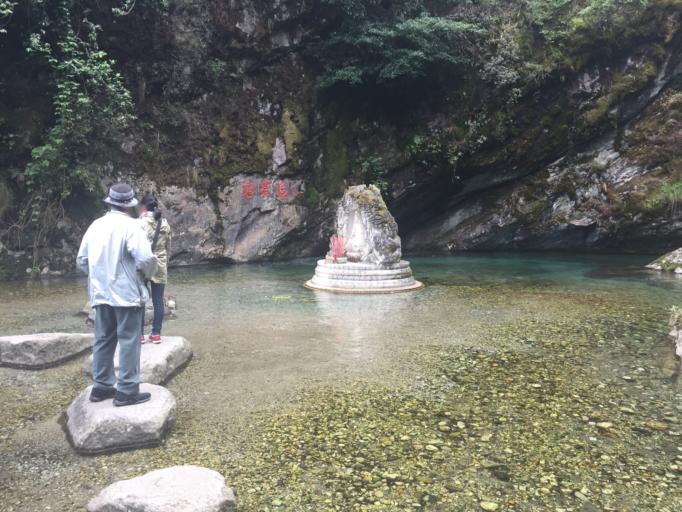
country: CN
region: Yunnan
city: Dali
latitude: 25.6473
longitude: 100.1424
